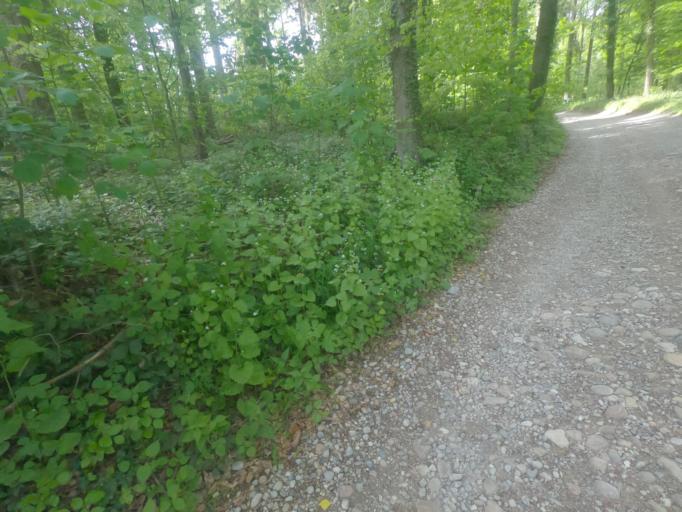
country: CH
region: Solothurn
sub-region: Bezirk Lebern
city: Riedholz
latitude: 47.2261
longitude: 7.5712
